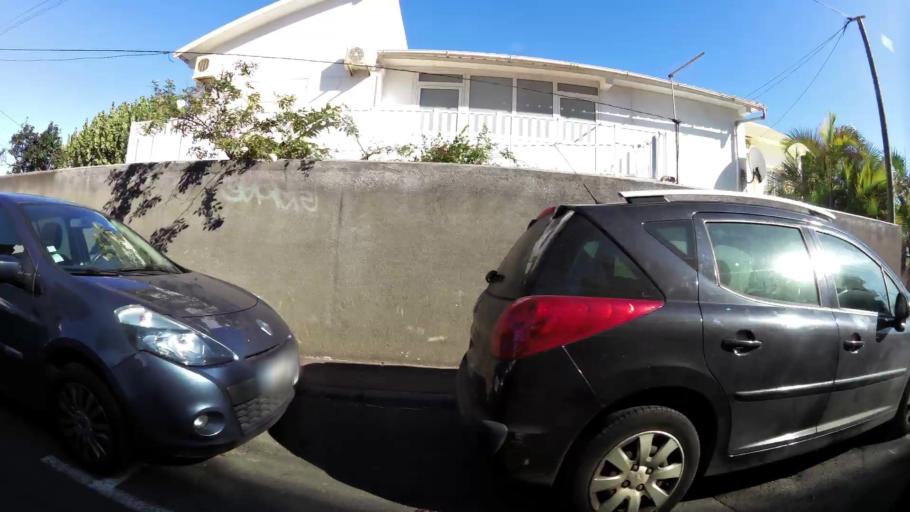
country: RE
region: Reunion
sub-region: Reunion
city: Saint-Pierre
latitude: -21.3401
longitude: 55.4668
